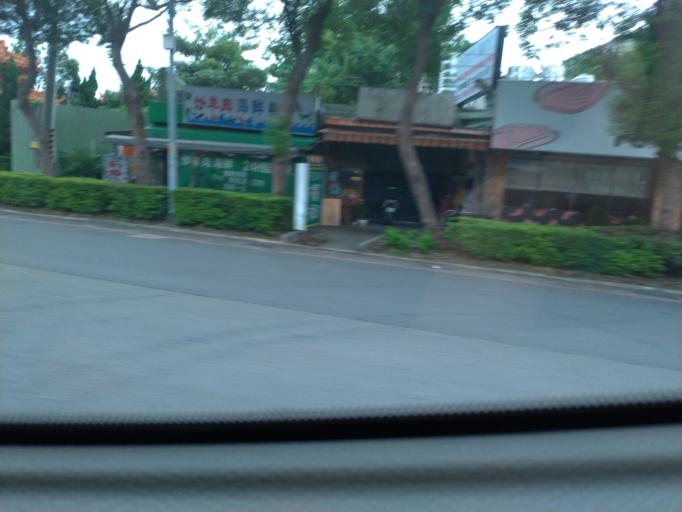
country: TW
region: Taiwan
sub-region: Taoyuan
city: Taoyuan
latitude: 24.9320
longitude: 121.3759
